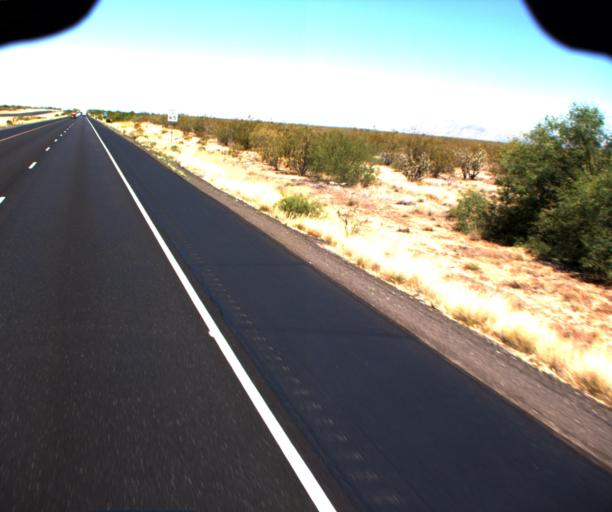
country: US
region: Arizona
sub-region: Yavapai County
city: Congress
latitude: 34.0580
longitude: -112.8565
